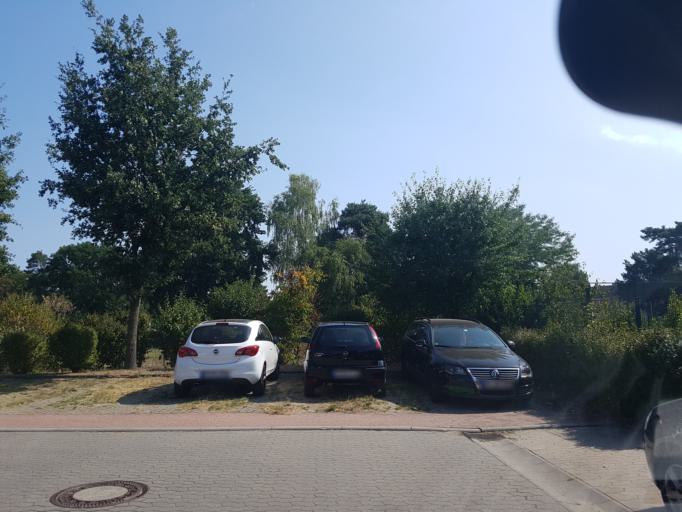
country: DE
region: Brandenburg
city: Treuenbrietzen
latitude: 52.0903
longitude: 12.8484
